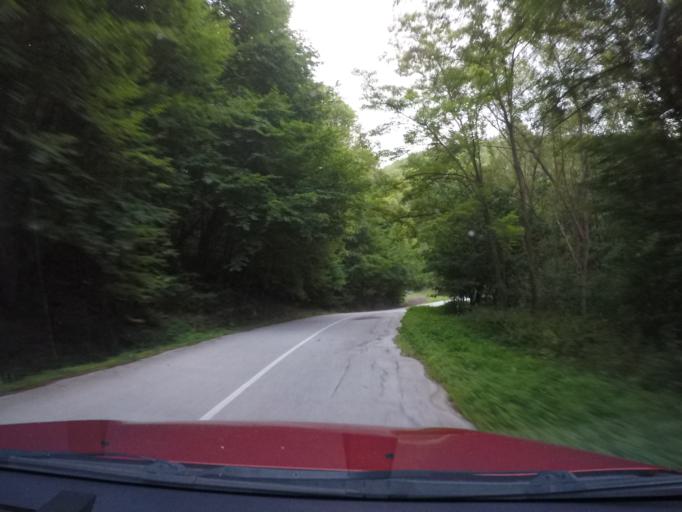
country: SK
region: Kosicky
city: Medzev
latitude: 48.6308
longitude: 20.7236
